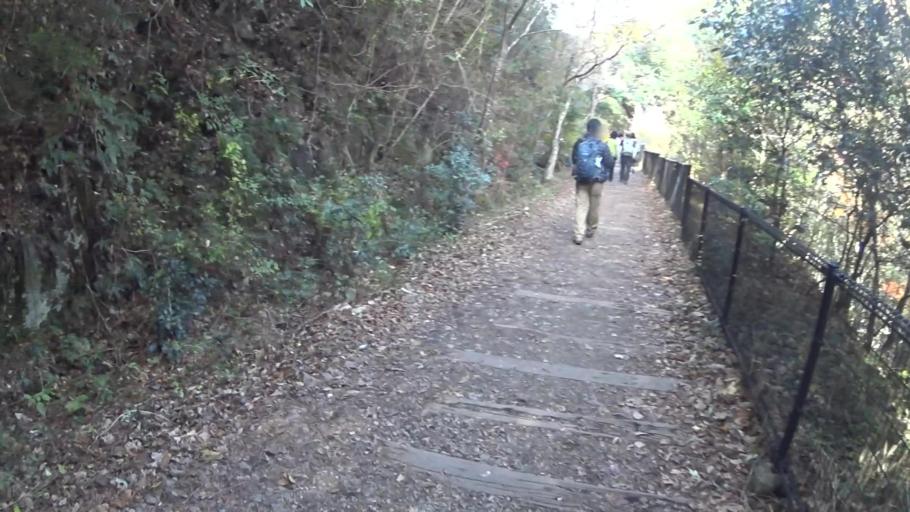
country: JP
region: Hyogo
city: Takarazuka
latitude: 34.8427
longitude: 135.3182
